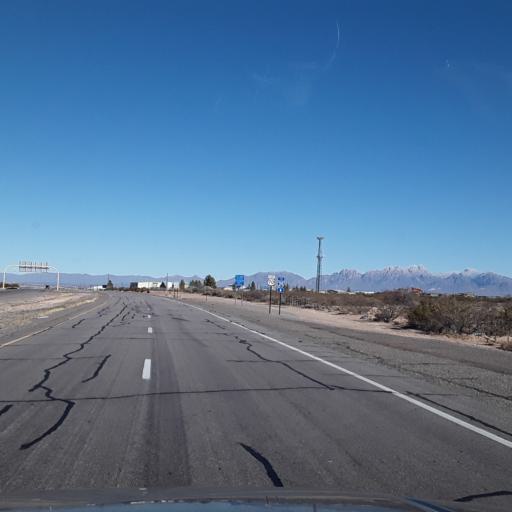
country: US
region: New Mexico
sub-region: Dona Ana County
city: Mesilla
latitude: 32.2844
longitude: -106.8792
